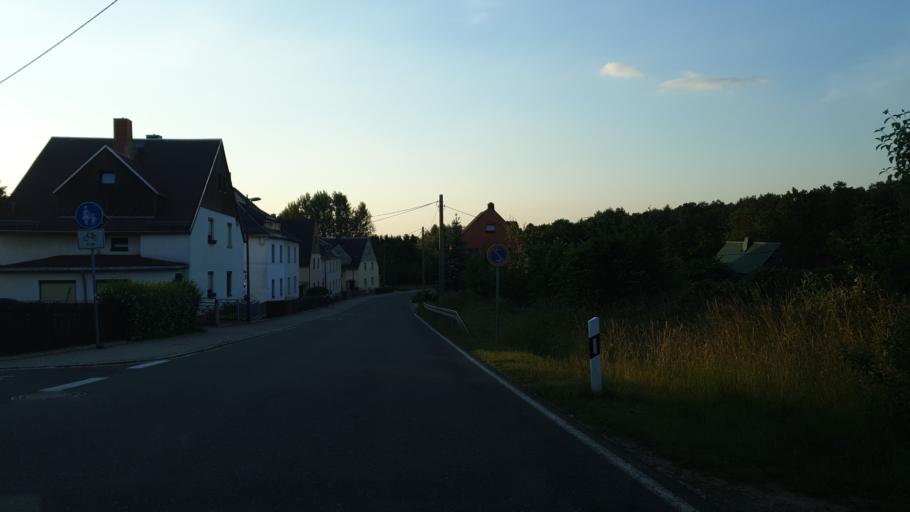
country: DE
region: Saxony
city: Oelsnitz
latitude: 50.7095
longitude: 12.7094
